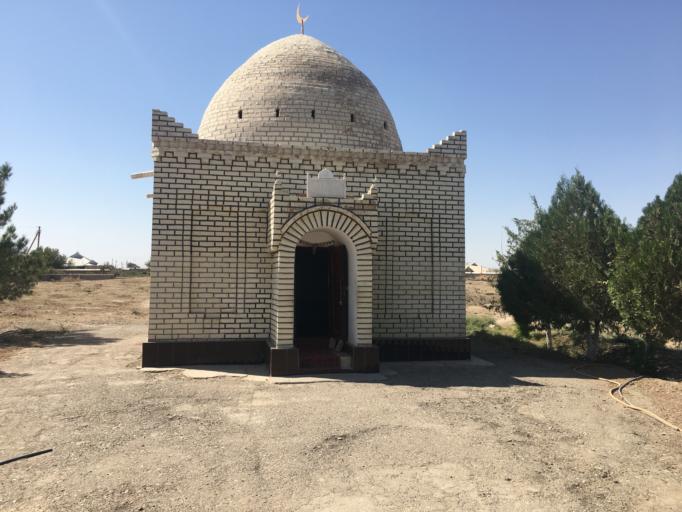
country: IR
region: Razavi Khorasan
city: Sarakhs
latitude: 36.5148
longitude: 61.2153
